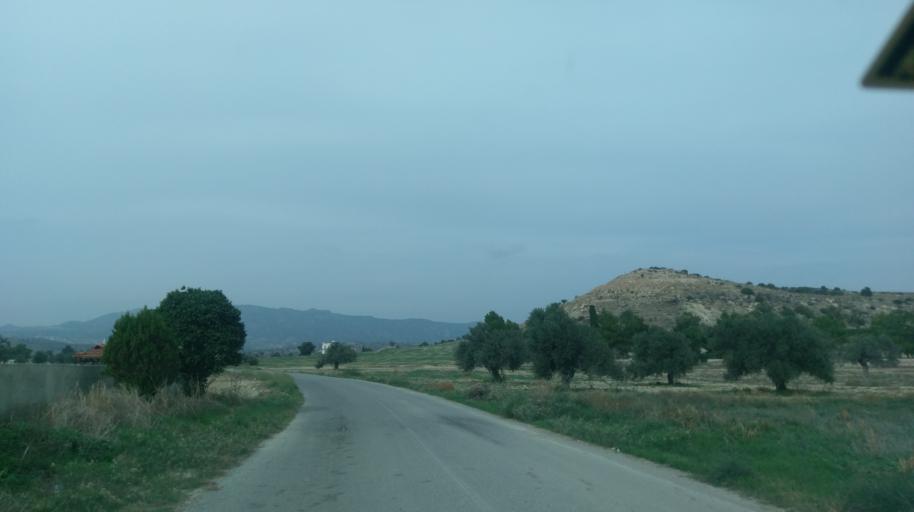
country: CY
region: Ammochostos
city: Trikomo
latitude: 35.3234
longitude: 33.9345
